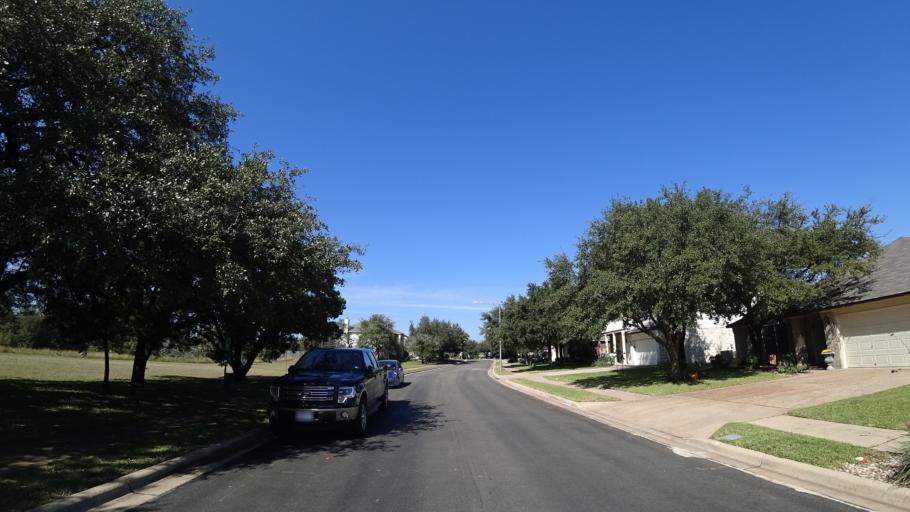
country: US
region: Texas
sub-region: Travis County
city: Shady Hollow
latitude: 30.1952
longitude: -97.8638
